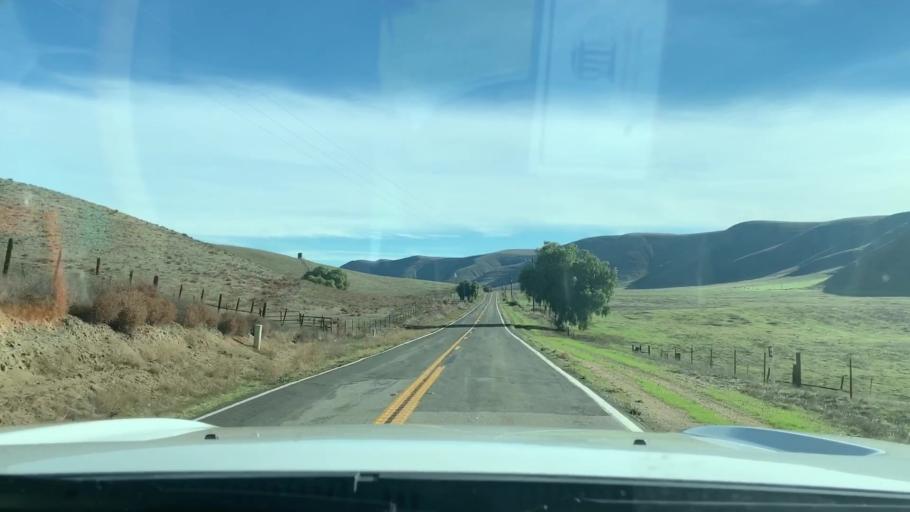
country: US
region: California
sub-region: Monterey County
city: King City
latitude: 36.1501
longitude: -120.9399
